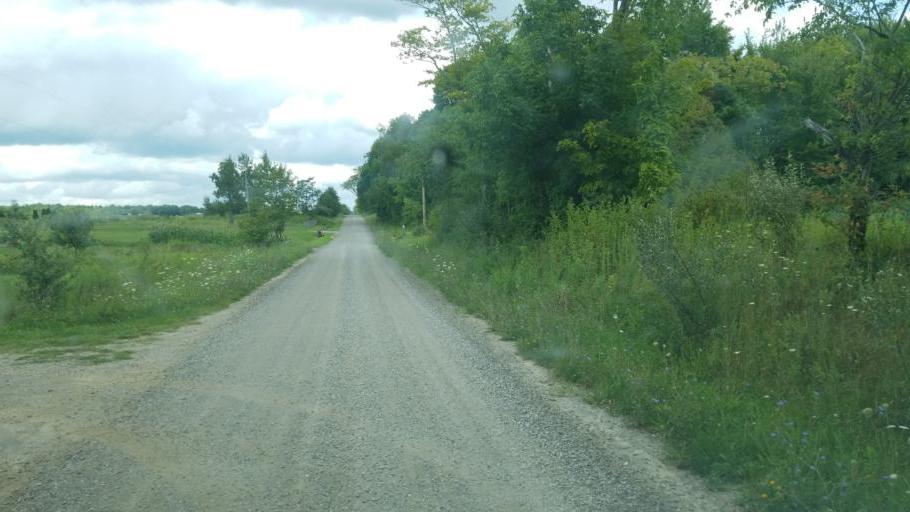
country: US
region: Ohio
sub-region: Ashtabula County
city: Andover
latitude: 41.5933
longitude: -80.6852
